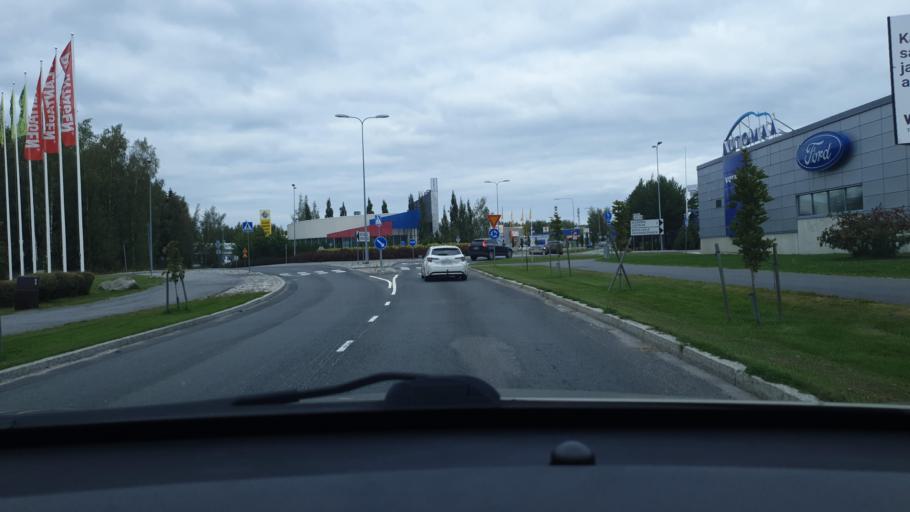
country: FI
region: Ostrobothnia
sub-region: Vaasa
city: Korsholm
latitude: 63.1080
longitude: 21.6484
